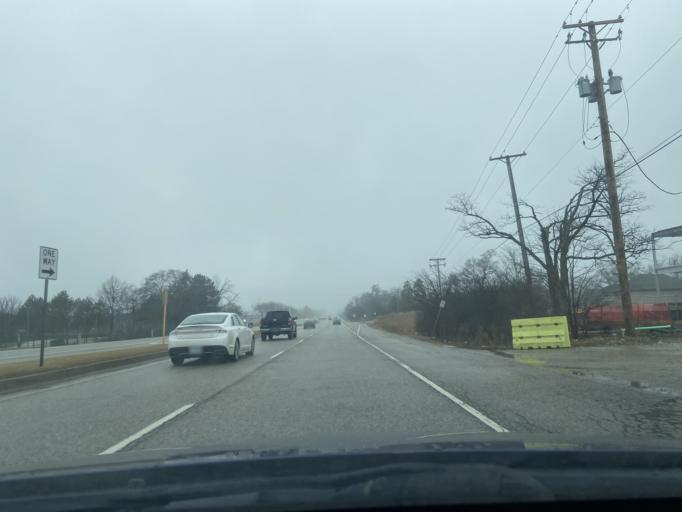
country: US
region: Illinois
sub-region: Lake County
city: Knollwood
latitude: 42.2038
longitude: -88.1115
